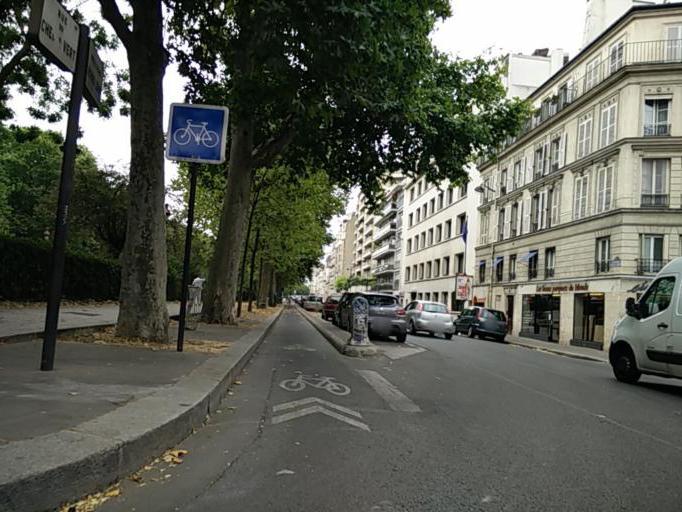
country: FR
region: Ile-de-France
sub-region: Paris
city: Paris
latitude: 48.8579
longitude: 2.3710
